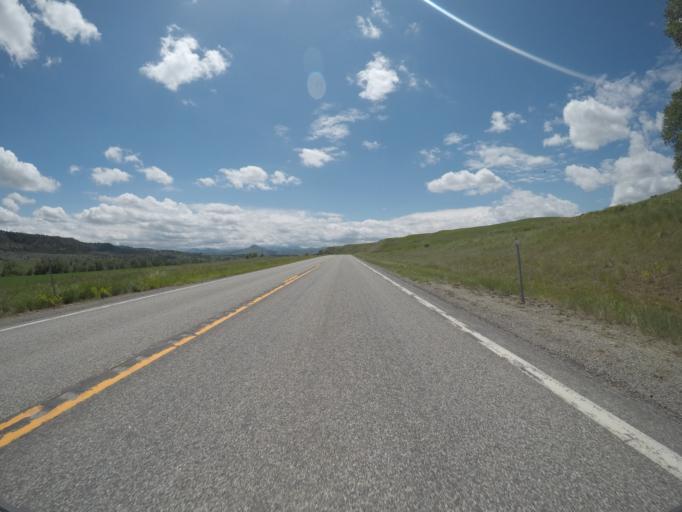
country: US
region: Montana
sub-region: Sweet Grass County
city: Big Timber
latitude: 45.7551
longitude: -109.9923
